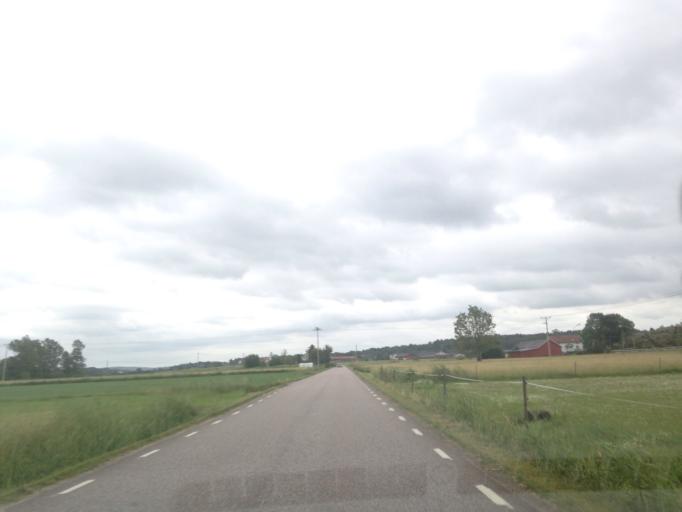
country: SE
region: Vaestra Goetaland
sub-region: Kungalvs Kommun
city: Kode
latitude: 57.8257
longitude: 11.8187
